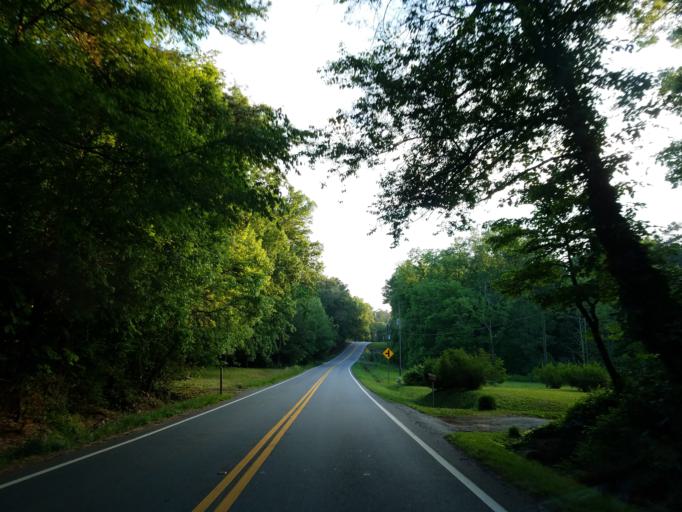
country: US
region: Georgia
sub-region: Cherokee County
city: Canton
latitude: 34.2144
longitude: -84.5075
